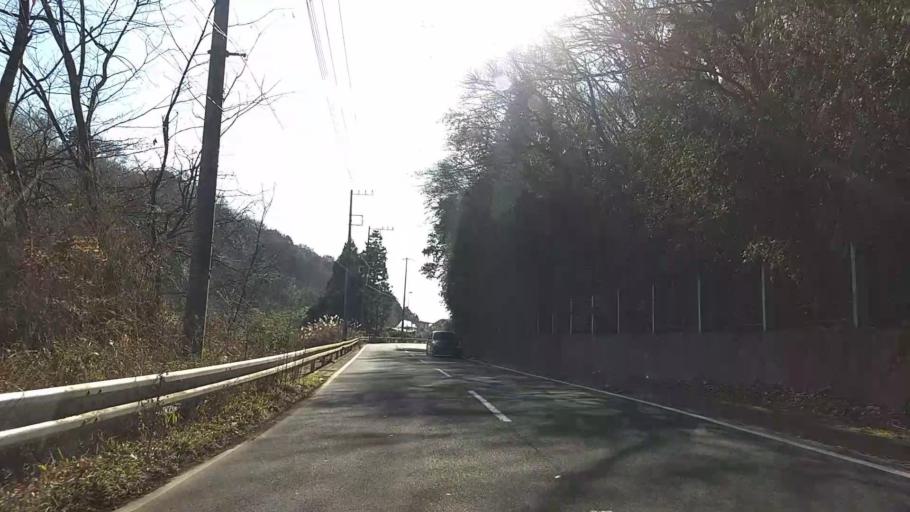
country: JP
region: Kanagawa
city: Isehara
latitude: 35.4594
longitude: 139.2910
